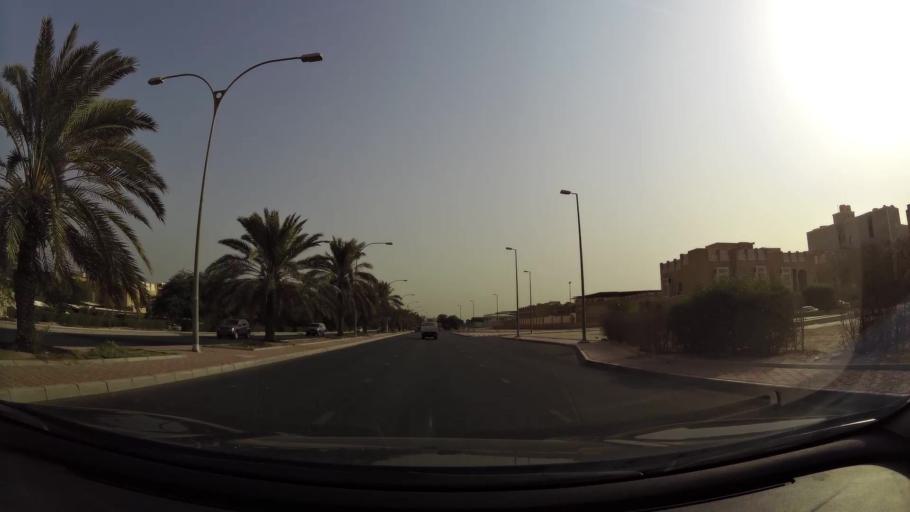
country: KW
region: Al Ahmadi
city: Ar Riqqah
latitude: 29.1314
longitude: 48.1033
